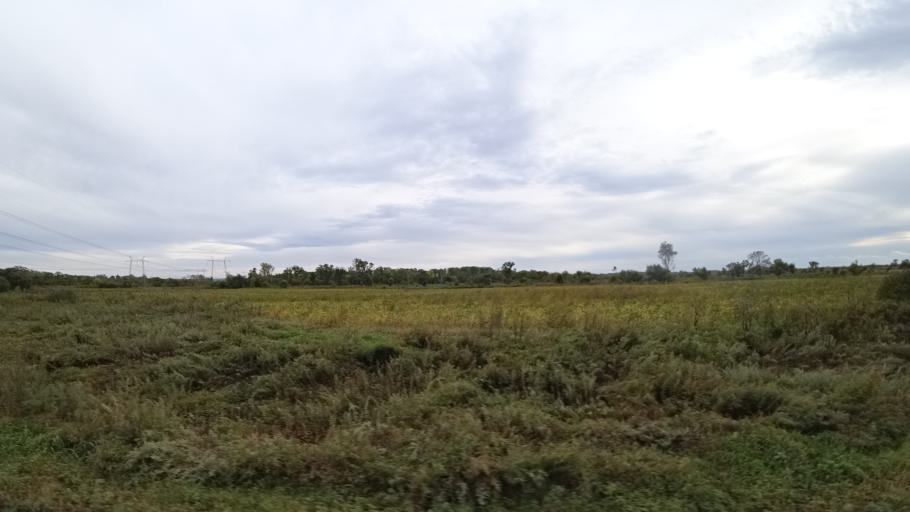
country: RU
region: Amur
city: Arkhara
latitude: 49.4298
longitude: 130.2494
